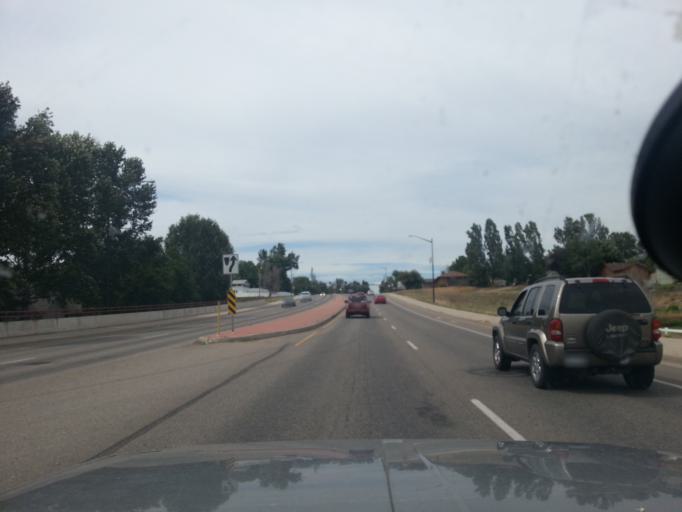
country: US
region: Colorado
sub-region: Larimer County
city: Loveland
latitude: 40.3976
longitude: -105.0968
